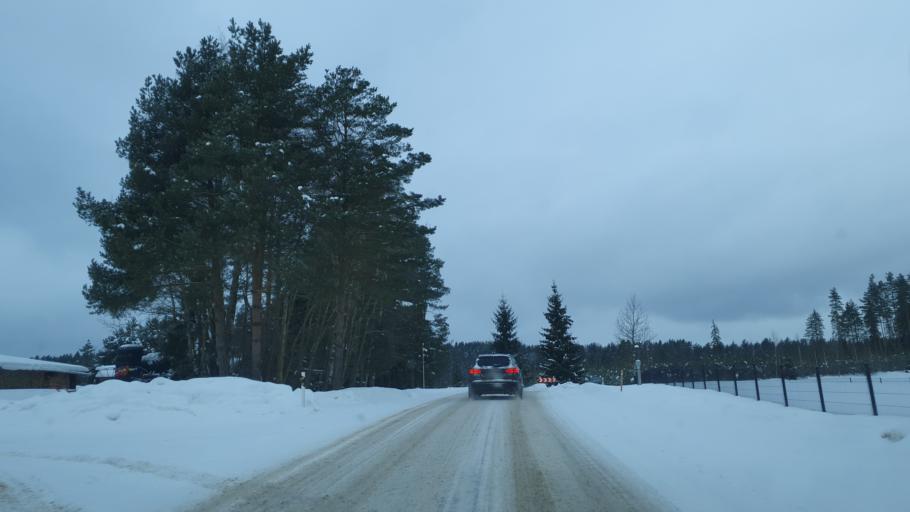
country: EE
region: Polvamaa
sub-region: Polva linn
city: Polva
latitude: 58.1060
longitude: 27.0880
